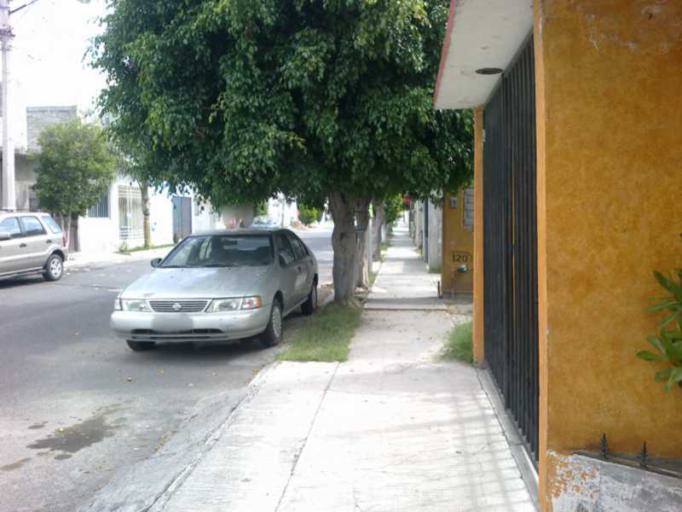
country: MX
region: Queretaro
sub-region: Queretaro
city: Sergio Villasenor
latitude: 20.6260
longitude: -100.3992
